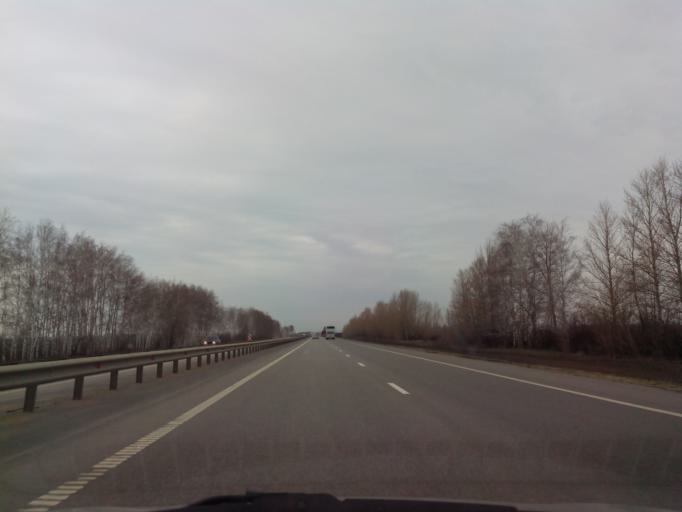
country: RU
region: Tambov
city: Selezni
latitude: 52.8094
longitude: 40.9586
